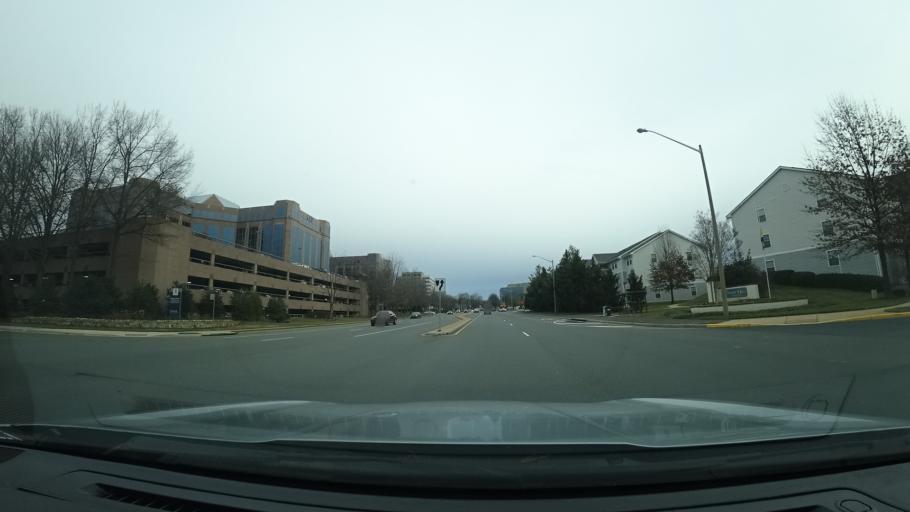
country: US
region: Virginia
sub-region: Fairfax County
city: Floris
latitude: 38.9564
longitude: -77.4241
